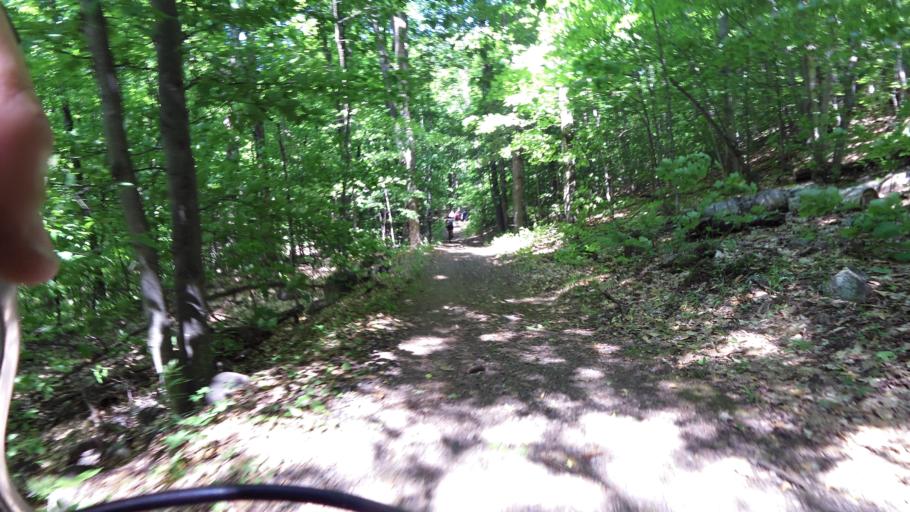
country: CA
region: Quebec
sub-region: Outaouais
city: Wakefield
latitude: 45.5540
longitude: -75.8961
